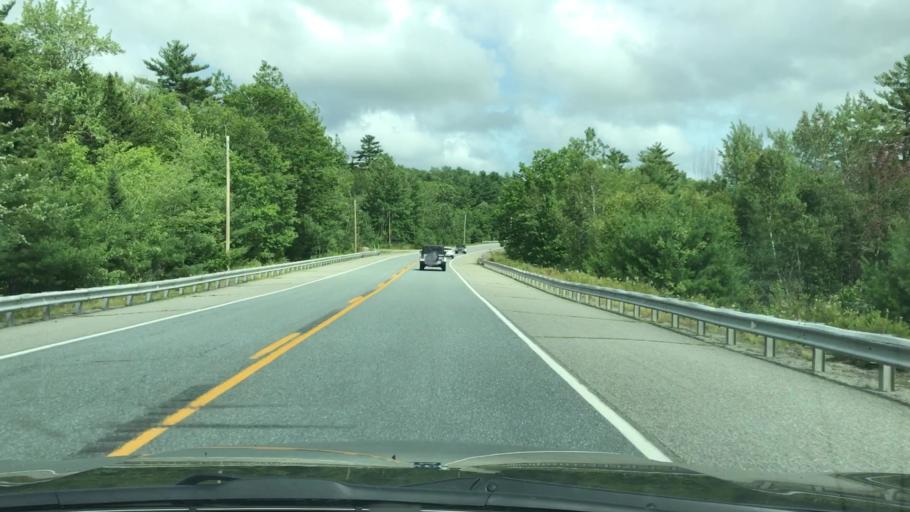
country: US
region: Maine
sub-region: Hancock County
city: Surry
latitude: 44.5637
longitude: -68.5926
